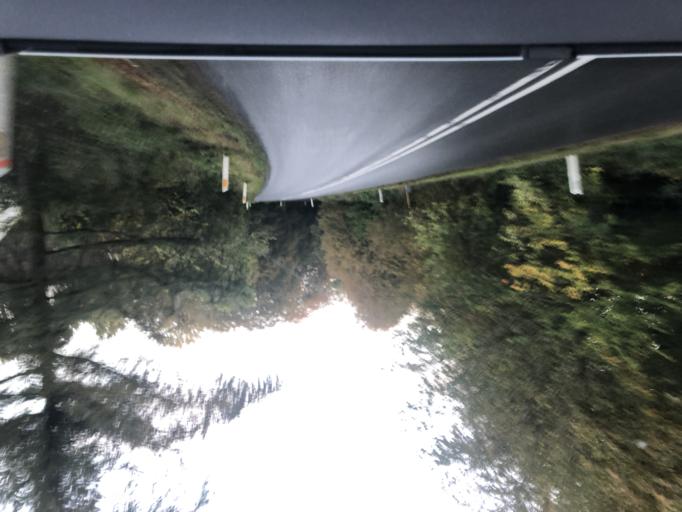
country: DK
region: Capital Region
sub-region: Egedal Kommune
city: Stenlose
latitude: 55.8091
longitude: 12.2097
